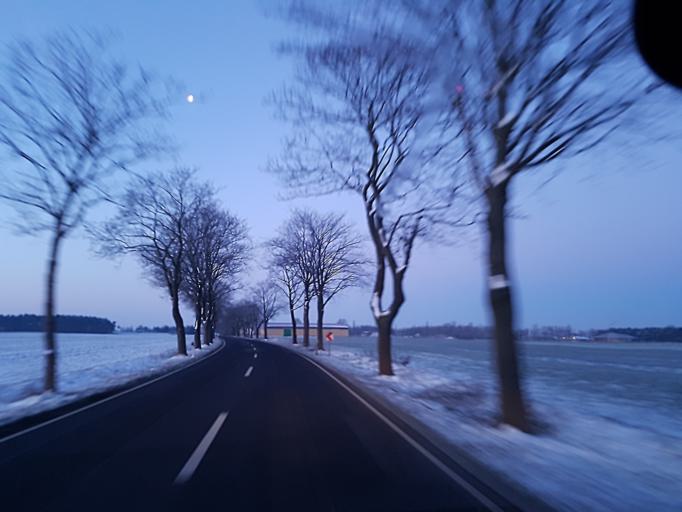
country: DE
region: Brandenburg
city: Muhlberg
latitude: 51.4556
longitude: 13.2410
